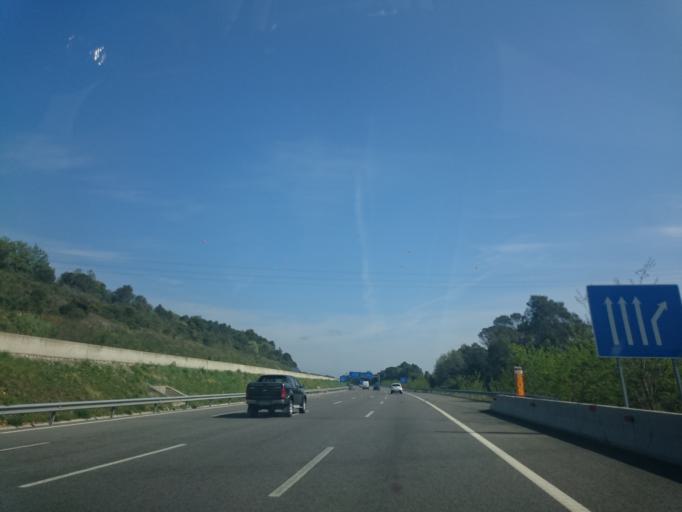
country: ES
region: Catalonia
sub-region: Provincia de Girona
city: Cervia de Ter
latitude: 42.0632
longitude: 2.8860
